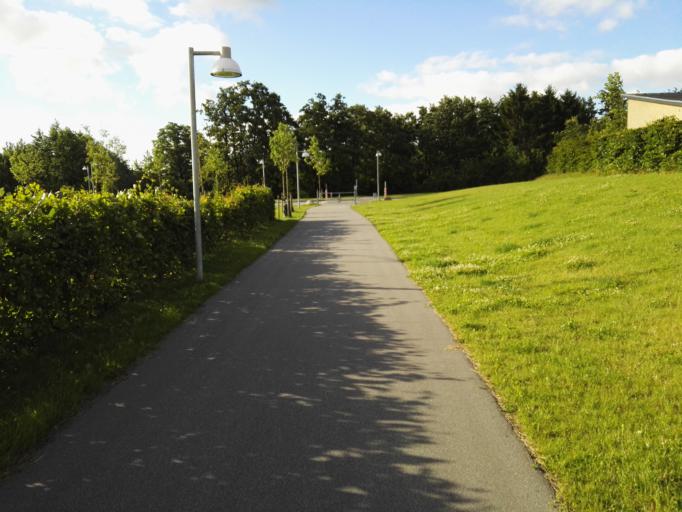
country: DK
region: Capital Region
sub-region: Ballerup Kommune
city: Malov
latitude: 55.7428
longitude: 12.3206
